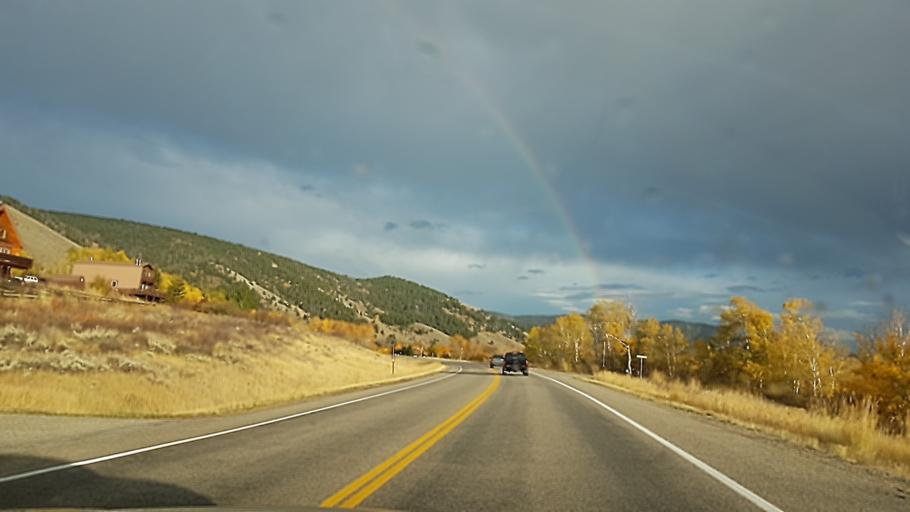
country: US
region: Montana
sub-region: Gallatin County
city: West Yellowstone
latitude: 44.6632
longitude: -111.3818
